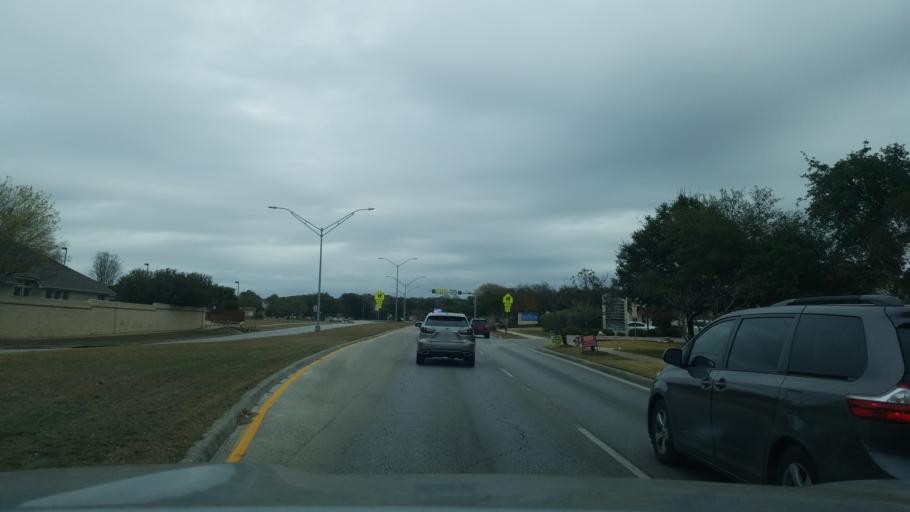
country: US
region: Texas
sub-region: Bexar County
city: Shavano Park
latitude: 29.5857
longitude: -98.5328
